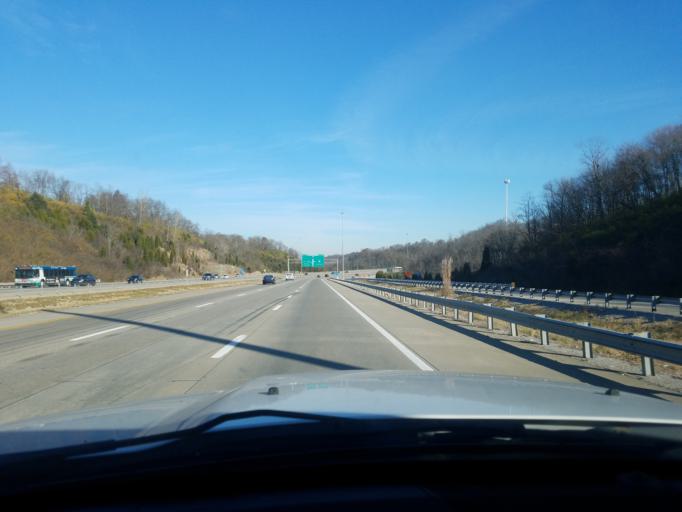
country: US
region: Kentucky
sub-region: Campbell County
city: Highland Heights
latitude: 39.0376
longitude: -84.4700
